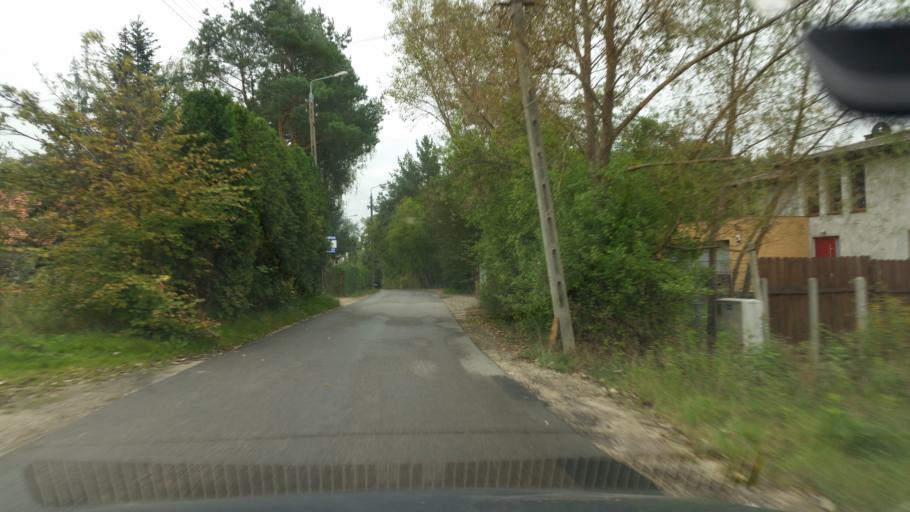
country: PL
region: Masovian Voivodeship
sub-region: Powiat piaseczynski
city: Jozefoslaw
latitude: 52.0900
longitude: 21.0798
